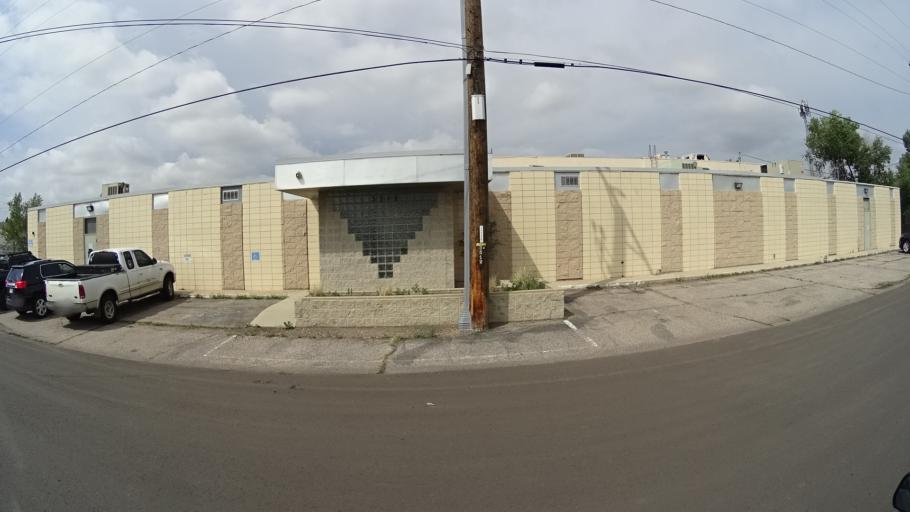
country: US
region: Colorado
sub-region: El Paso County
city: Colorado Springs
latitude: 38.8804
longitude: -104.8211
